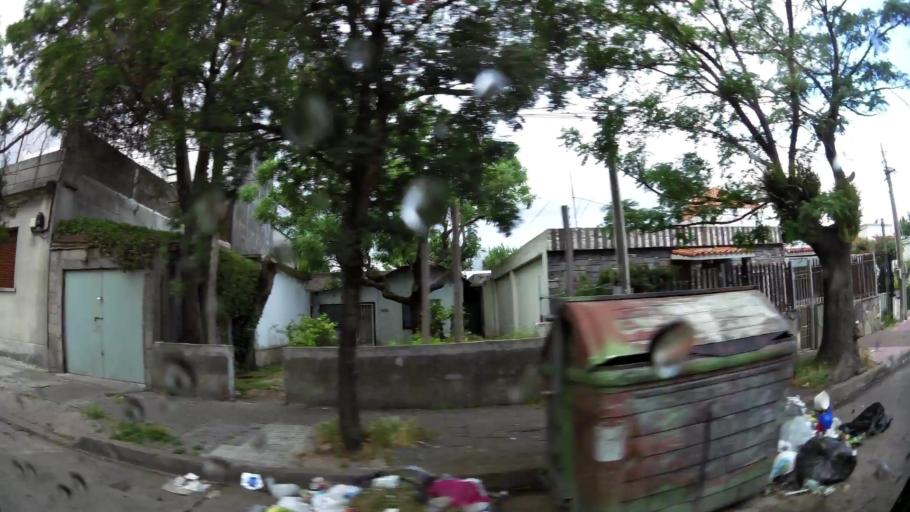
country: UY
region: Montevideo
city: Montevideo
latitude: -34.8547
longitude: -56.1676
